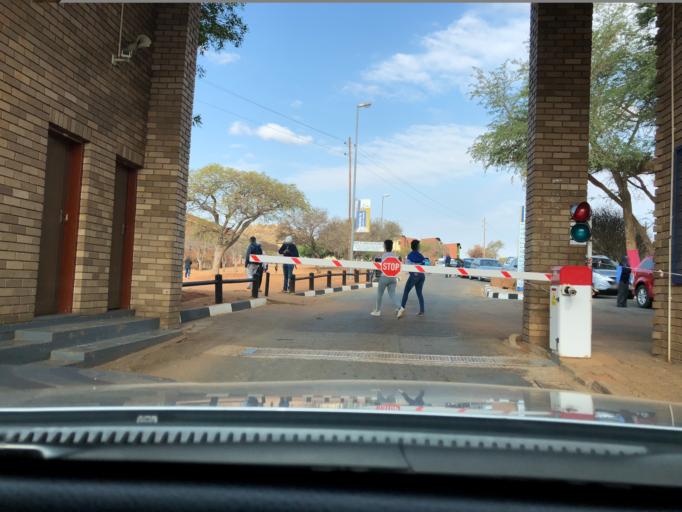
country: ZA
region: Limpopo
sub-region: Capricorn District Municipality
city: Mankoeng
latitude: -23.8925
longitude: 29.7336
